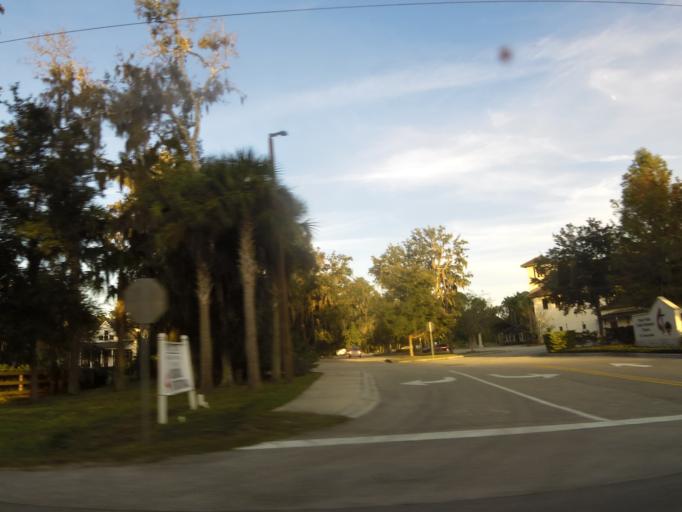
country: US
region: Florida
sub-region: Saint Johns County
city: Palm Valley
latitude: 30.1670
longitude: -81.3979
